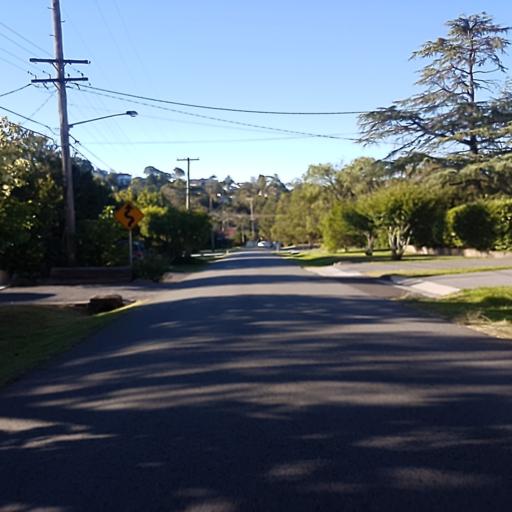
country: AU
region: New South Wales
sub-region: Ku-ring-gai
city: Roseville Chase
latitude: -33.7795
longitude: 151.2041
